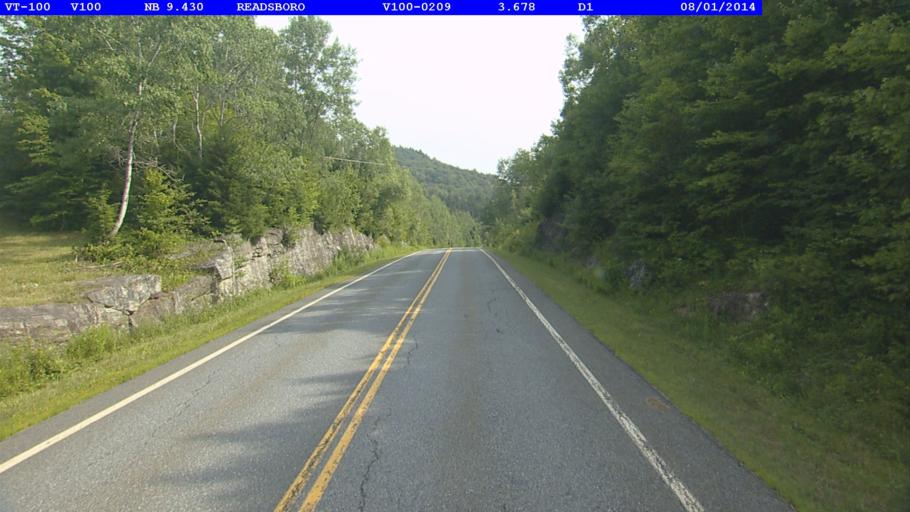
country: US
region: Massachusetts
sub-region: Berkshire County
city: North Adams
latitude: 42.8112
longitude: -72.9725
